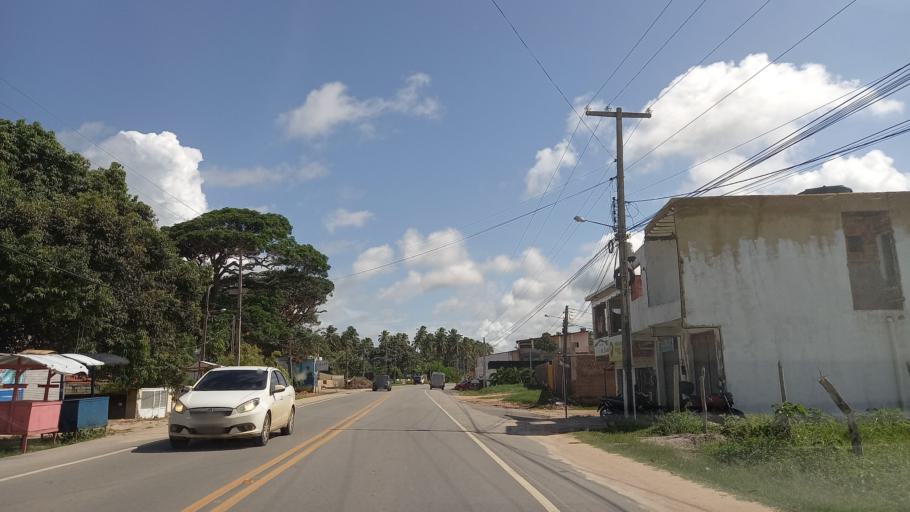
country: BR
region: Pernambuco
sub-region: Sao Jose Da Coroa Grande
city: Sao Jose da Coroa Grande
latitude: -8.9261
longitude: -35.1615
